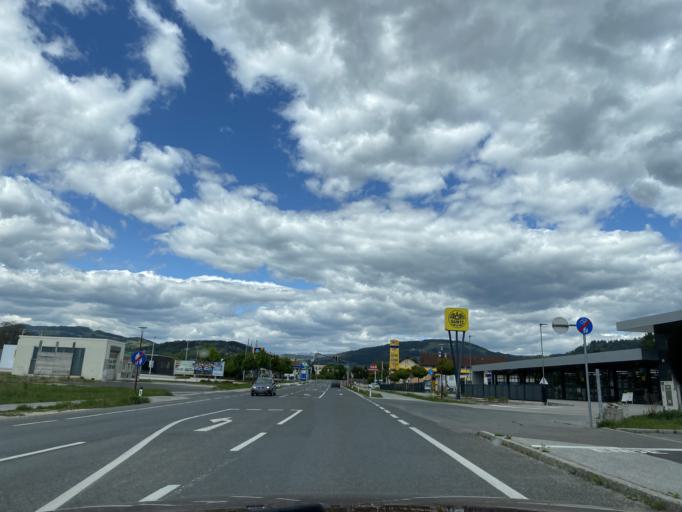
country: AT
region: Carinthia
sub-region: Politischer Bezirk Wolfsberg
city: Wolfsberg
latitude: 46.8258
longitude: 14.8395
